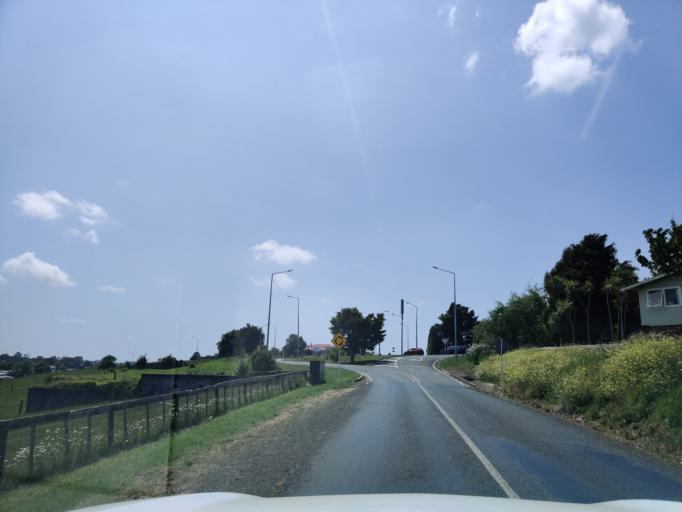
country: NZ
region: Auckland
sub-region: Auckland
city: Pukekohe East
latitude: -37.1978
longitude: 174.9225
